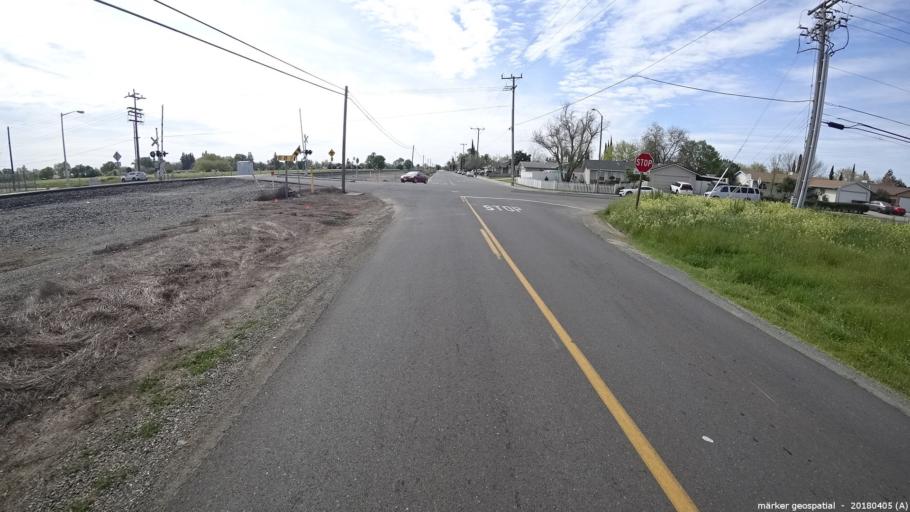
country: US
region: California
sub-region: Sacramento County
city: Galt
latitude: 38.2623
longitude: -121.3105
